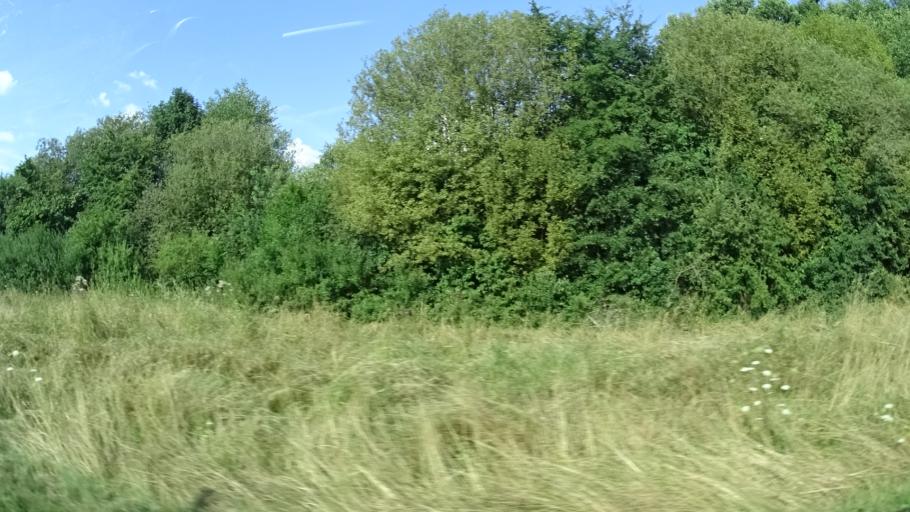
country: DE
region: Bavaria
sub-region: Regierungsbezirk Unterfranken
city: Oberelsbach
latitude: 50.3784
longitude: 10.1128
